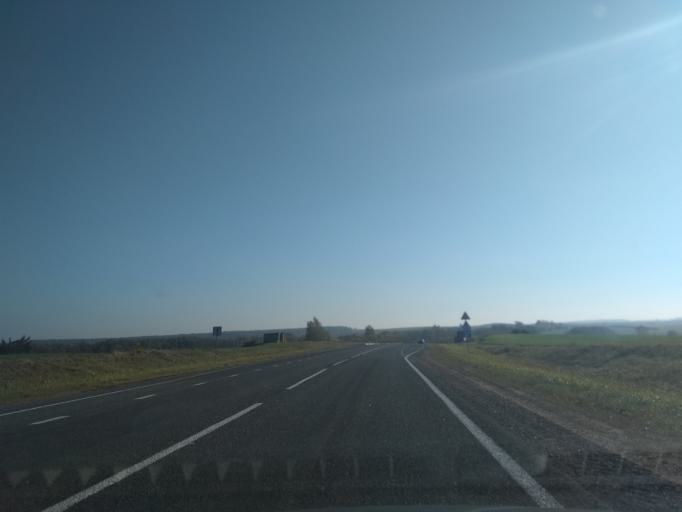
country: BY
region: Grodnenskaya
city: Zel'va
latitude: 53.1300
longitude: 25.0351
